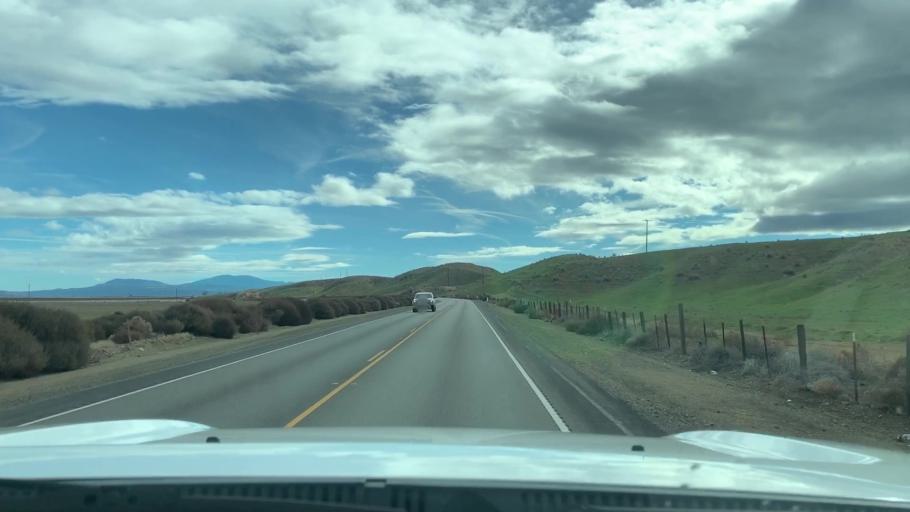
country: US
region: California
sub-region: Kern County
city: Taft Heights
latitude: 34.9686
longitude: -119.7418
